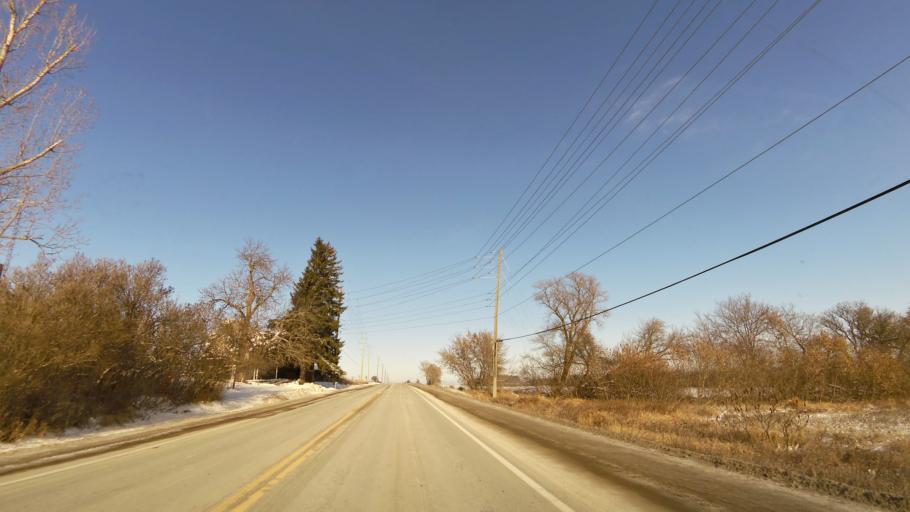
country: CA
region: Ontario
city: Quinte West
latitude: 44.1648
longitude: -77.8021
